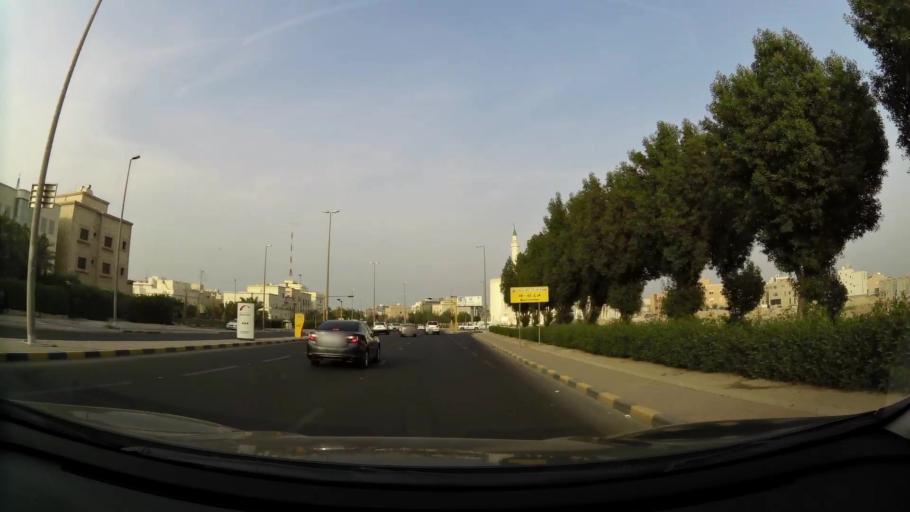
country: KW
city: Al Funaytis
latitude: 29.2283
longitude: 48.0833
